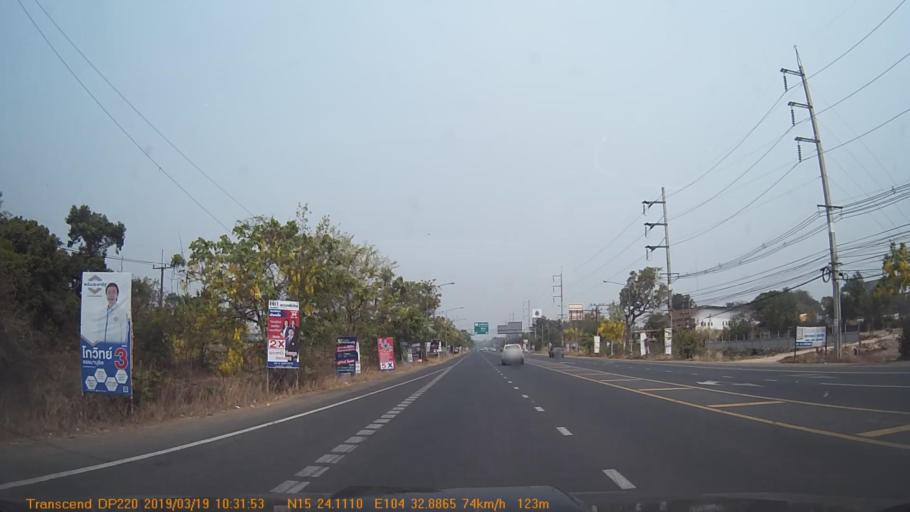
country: TH
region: Changwat Ubon Ratchathani
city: Khueang Nai
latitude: 15.4022
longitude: 104.5480
